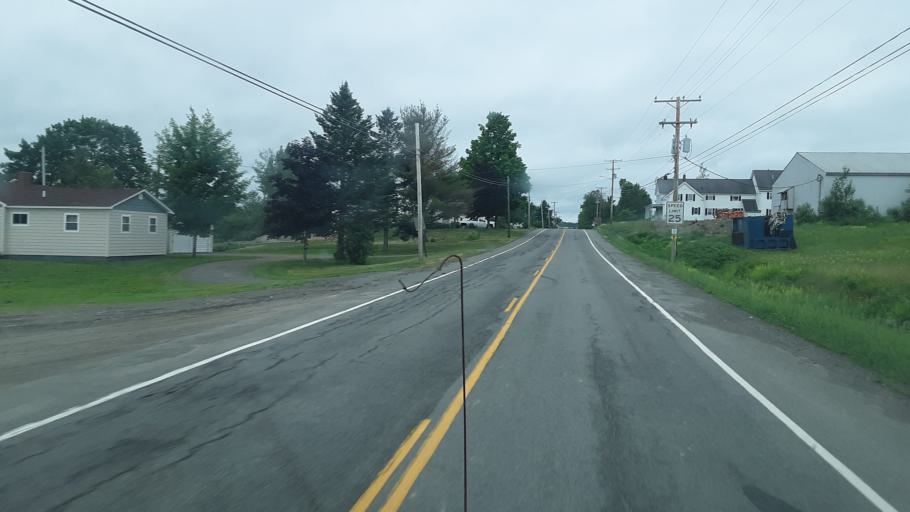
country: US
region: Maine
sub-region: Penobscot County
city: Patten
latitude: 46.0072
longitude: -68.4466
